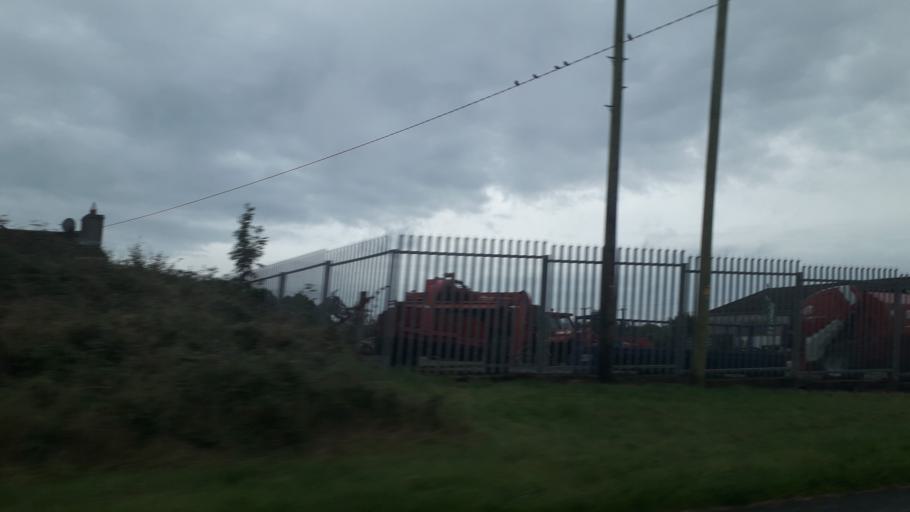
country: IE
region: Leinster
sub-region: An Longfort
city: Longford
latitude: 53.7256
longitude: -7.8724
